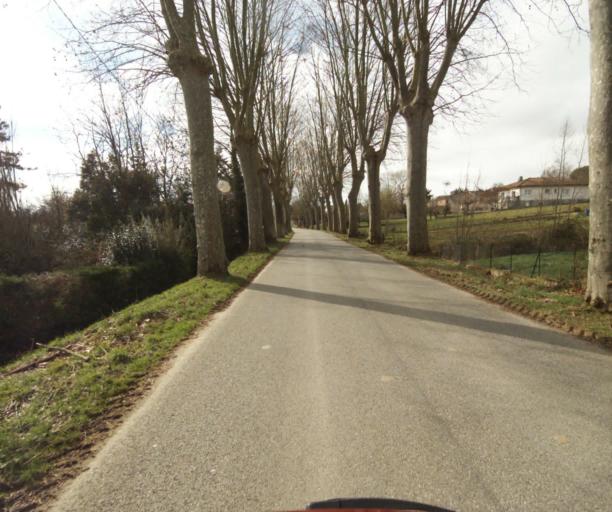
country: FR
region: Midi-Pyrenees
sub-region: Departement de l'Ariege
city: Pamiers
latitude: 43.1267
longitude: 1.5501
